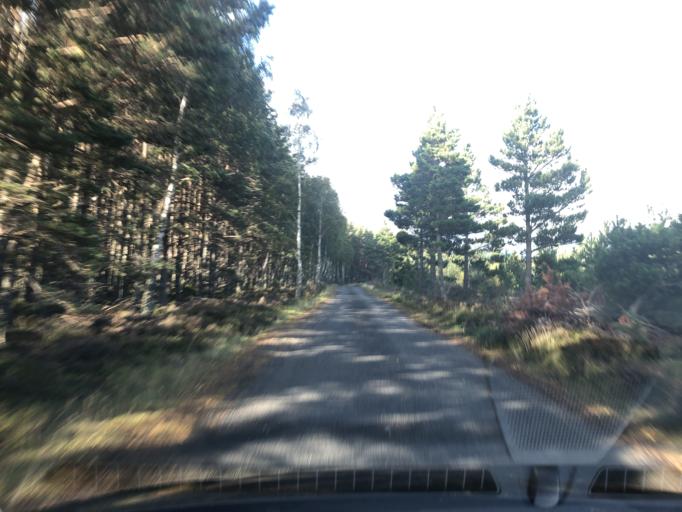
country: GB
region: Scotland
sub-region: Highland
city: Aviemore
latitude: 57.0686
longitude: -3.9015
